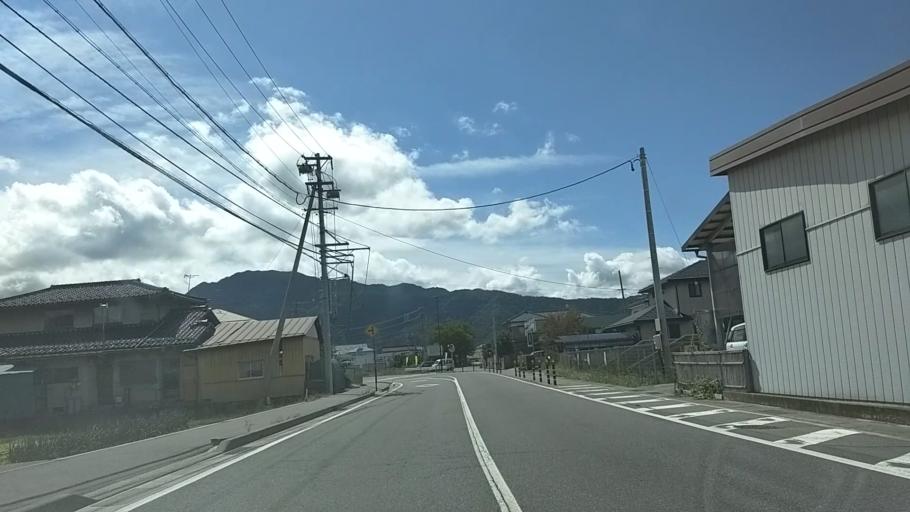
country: JP
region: Nagano
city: Suzaka
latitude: 36.6150
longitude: 138.2506
